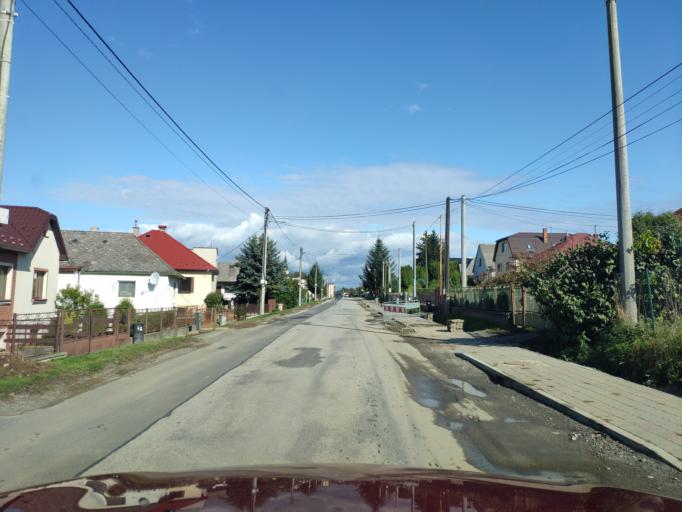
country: SK
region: Presovsky
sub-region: Okres Presov
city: Presov
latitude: 48.9142
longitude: 21.2603
